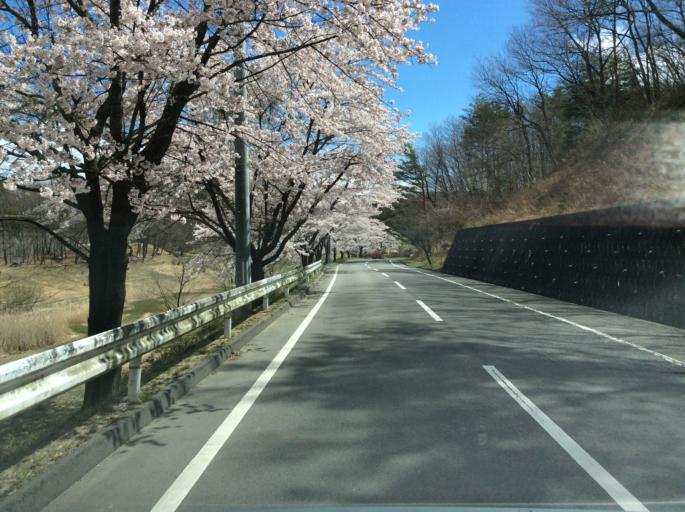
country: JP
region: Fukushima
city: Koriyama
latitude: 37.3510
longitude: 140.4275
